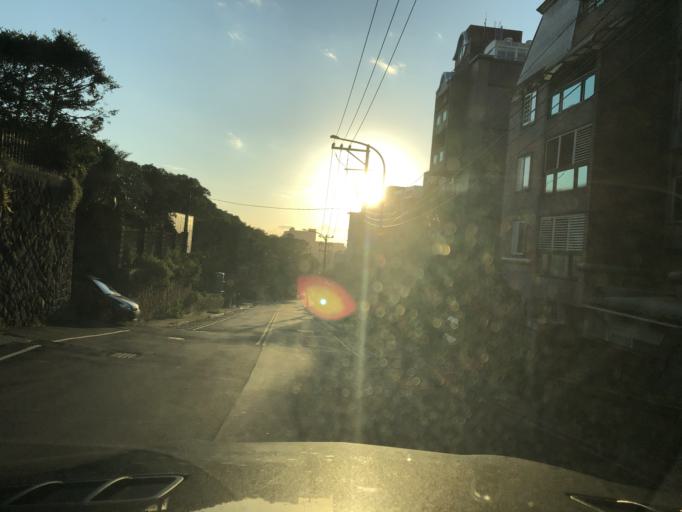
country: TW
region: Taipei
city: Taipei
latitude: 25.1396
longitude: 121.5506
